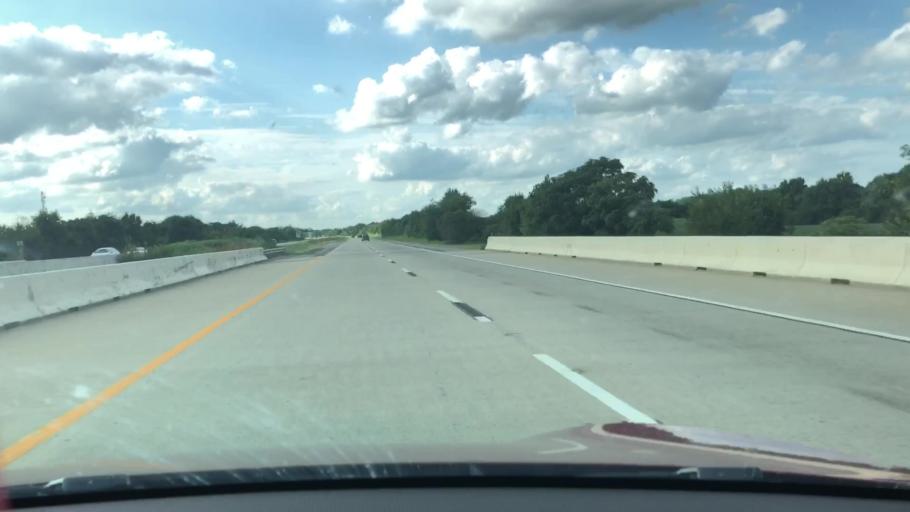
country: US
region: Delaware
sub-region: Kent County
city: Smyrna
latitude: 39.3112
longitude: -75.5976
